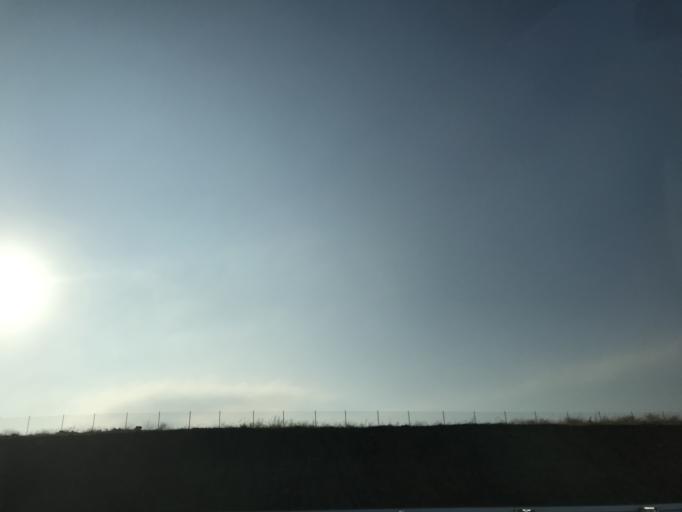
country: TR
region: Balikesir
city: Gobel
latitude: 40.0322
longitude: 28.2139
